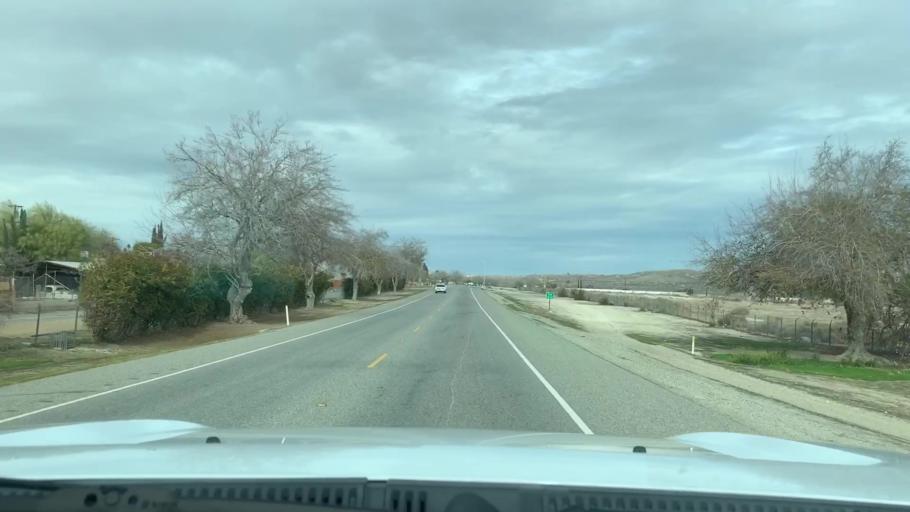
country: US
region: California
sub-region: Kern County
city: Taft
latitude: 35.1458
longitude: -119.4473
